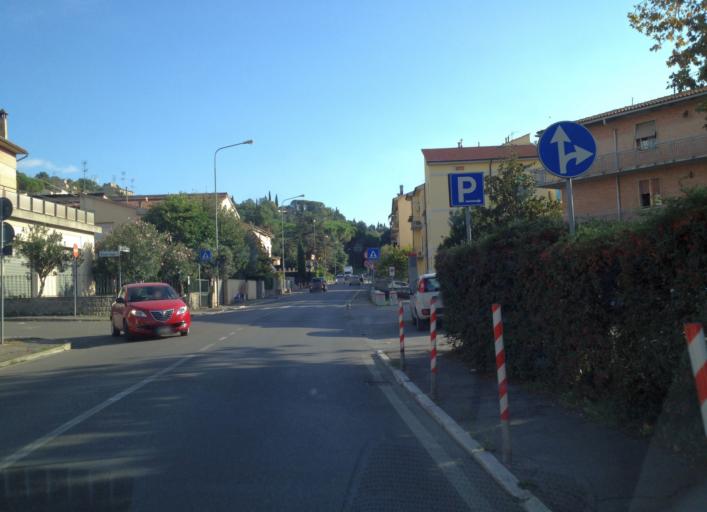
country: IT
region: Tuscany
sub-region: Provincia di Siena
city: Poggibonsi
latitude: 43.4670
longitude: 11.1440
